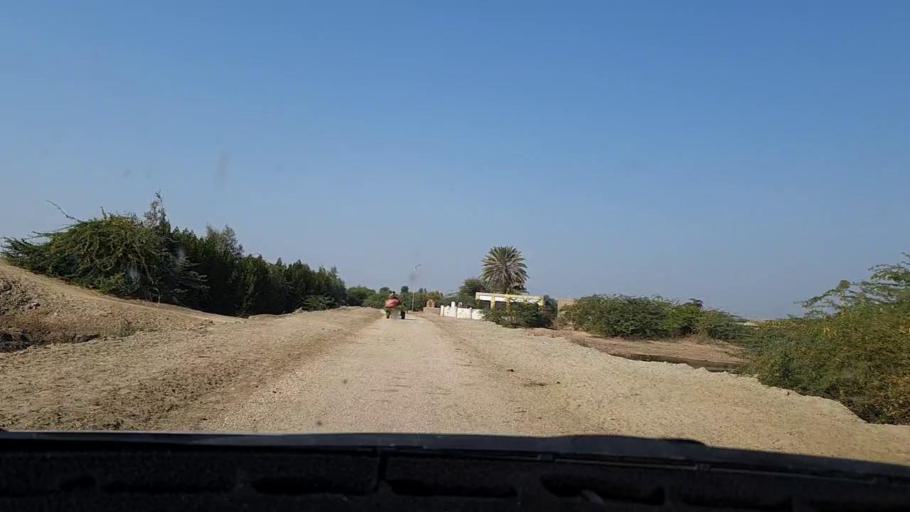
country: PK
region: Sindh
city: Tando Mittha Khan
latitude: 25.8297
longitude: 69.2883
